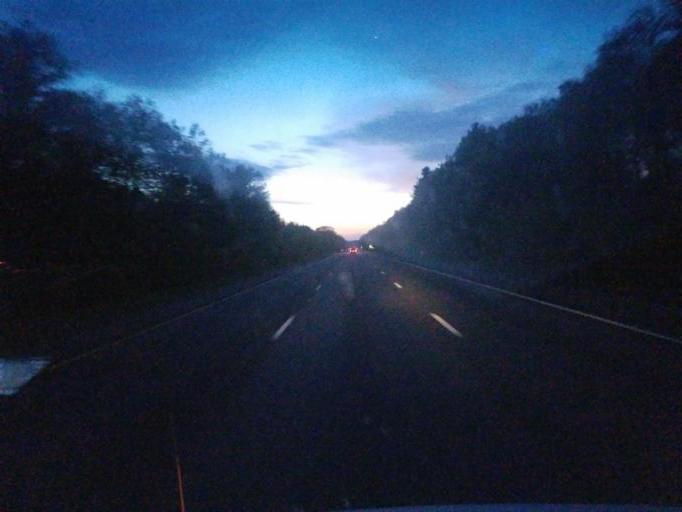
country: US
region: Massachusetts
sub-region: Worcester County
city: Bolton
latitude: 42.4561
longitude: -71.5748
